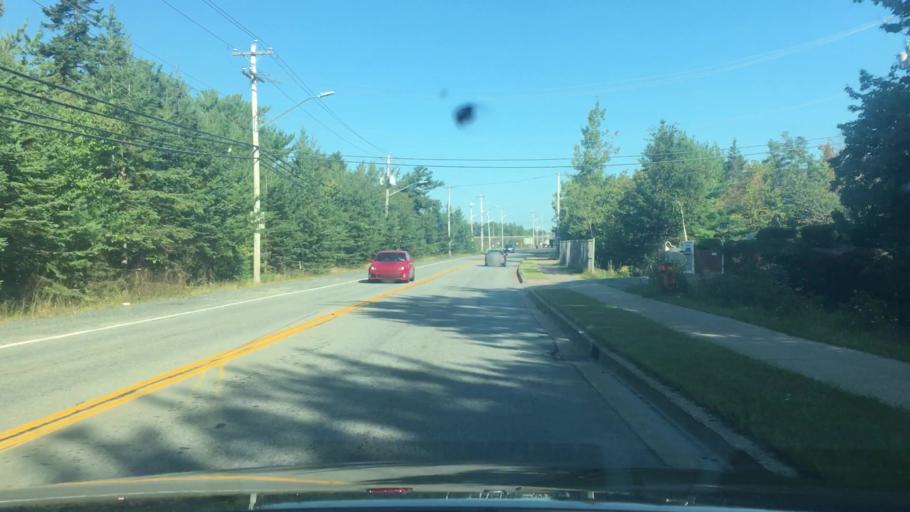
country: CA
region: Nova Scotia
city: Dartmouth
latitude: 44.7199
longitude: -63.6868
